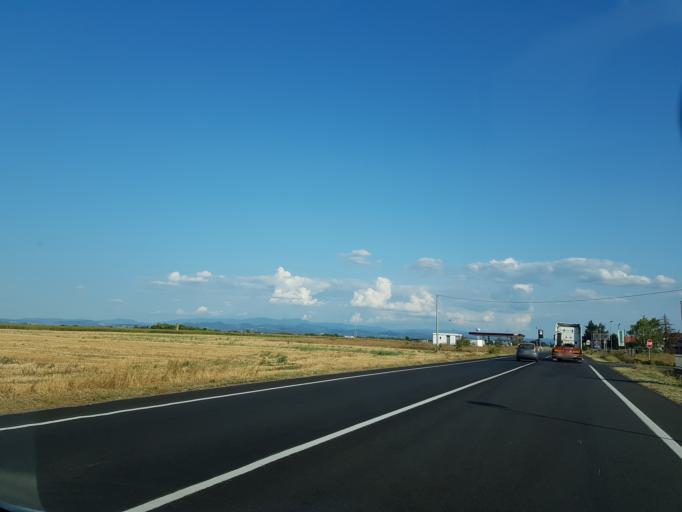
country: IT
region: Piedmont
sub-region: Provincia di Alessandria
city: Mandrogne
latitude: 44.8362
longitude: 8.7352
